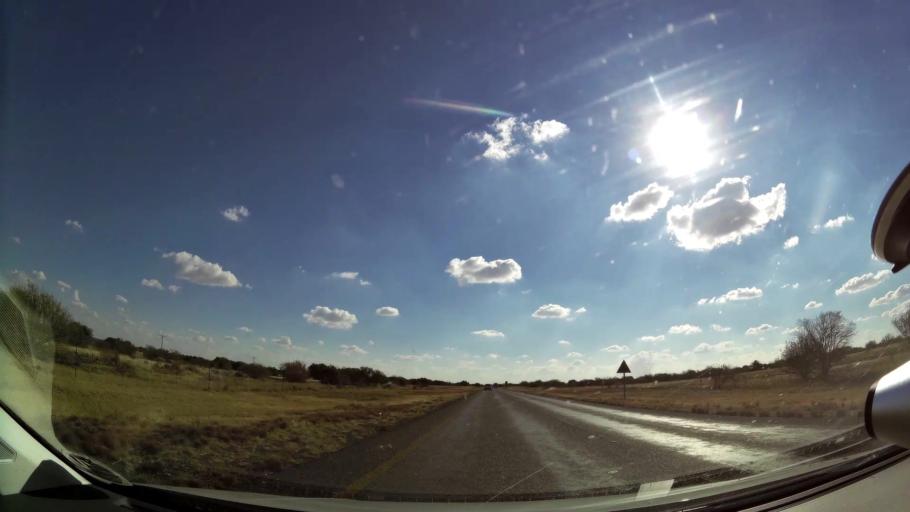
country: ZA
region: Northern Cape
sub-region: Frances Baard District Municipality
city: Kimberley
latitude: -28.8133
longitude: 24.8195
